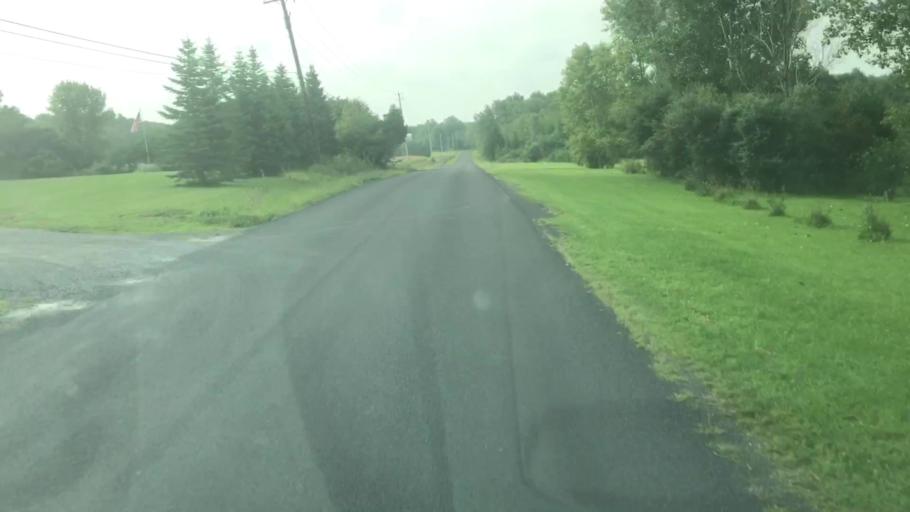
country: US
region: New York
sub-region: Onondaga County
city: Skaneateles
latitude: 42.9183
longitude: -76.4566
